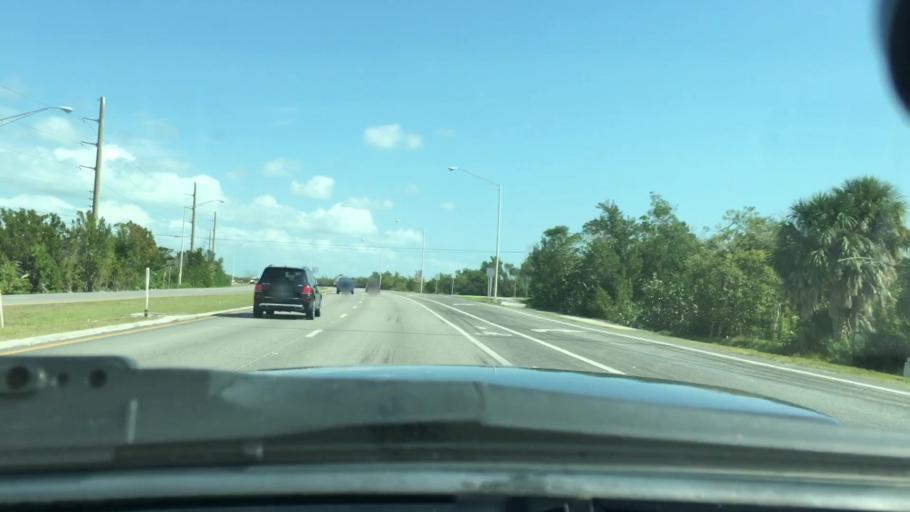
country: US
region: Florida
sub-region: Monroe County
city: Stock Island
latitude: 24.5789
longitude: -81.7085
